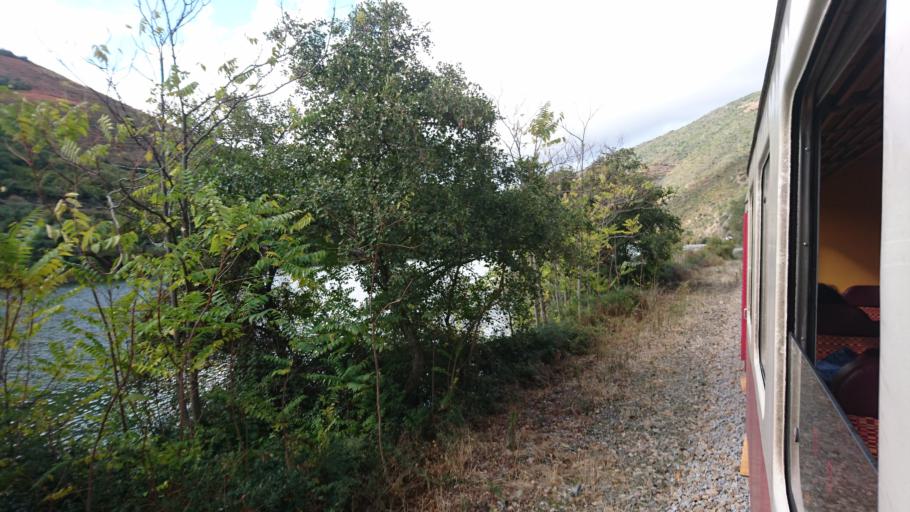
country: PT
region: Viseu
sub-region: Armamar
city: Armamar
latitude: 41.1625
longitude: -7.6525
